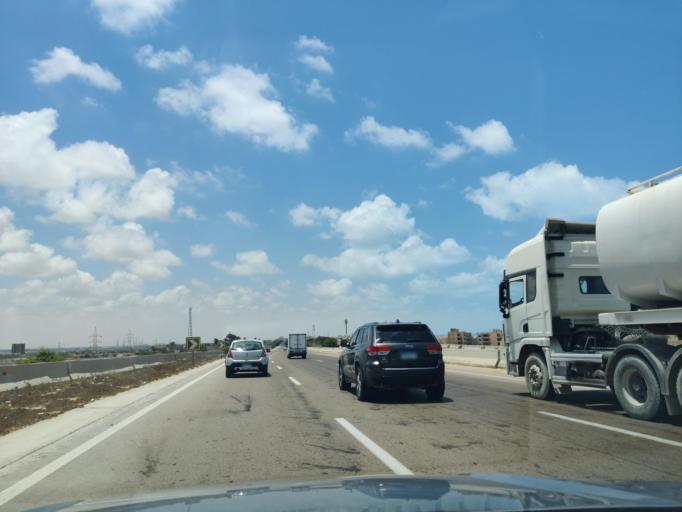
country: EG
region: Muhafazat Matruh
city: Al `Alamayn
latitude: 30.8300
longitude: 29.2145
